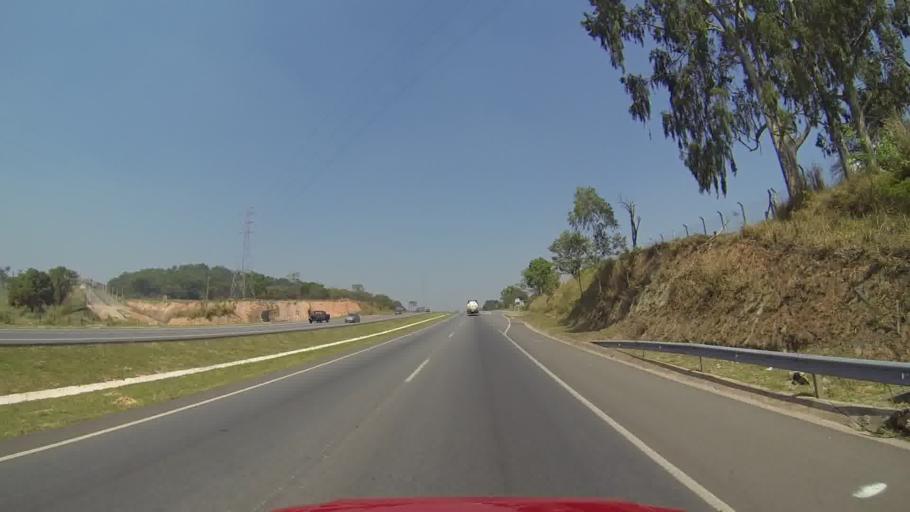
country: BR
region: Minas Gerais
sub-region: Belo Horizonte
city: Belo Horizonte
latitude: -19.9248
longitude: -43.9418
